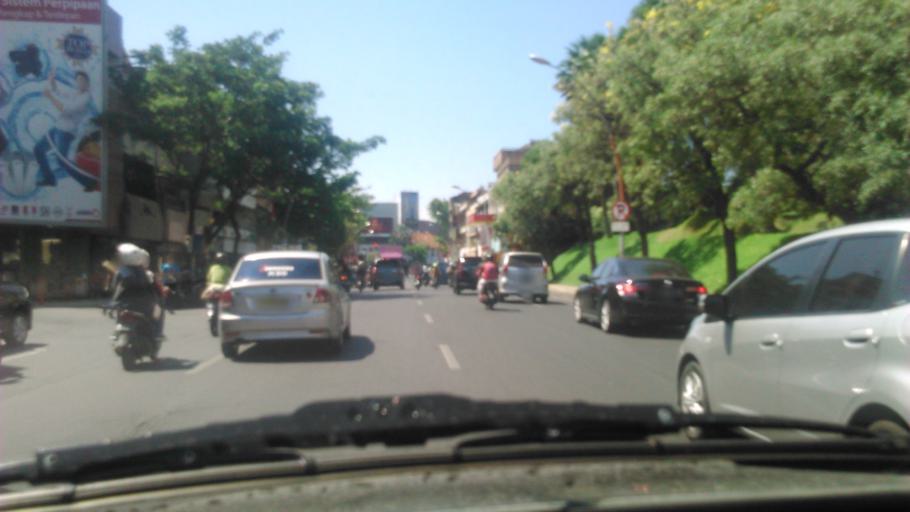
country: ID
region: East Java
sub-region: Kota Surabaya
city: Surabaya
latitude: -7.2580
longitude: 112.7333
